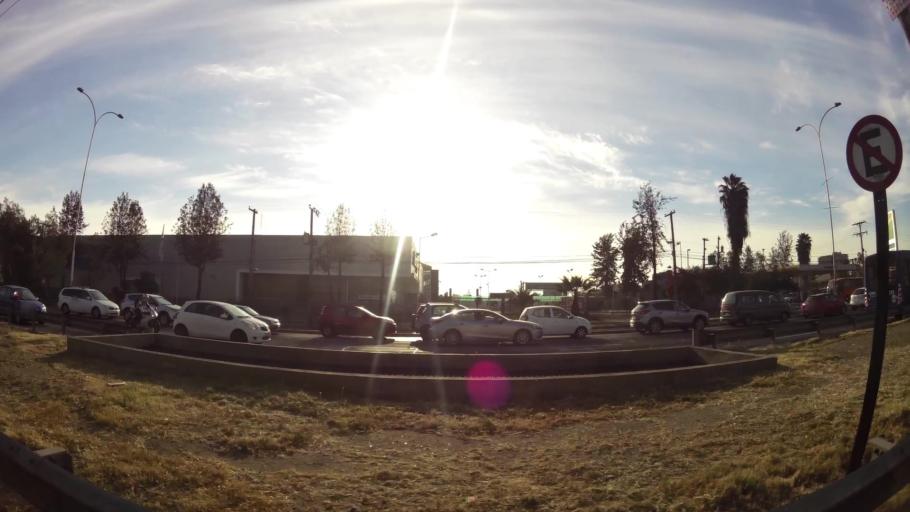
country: CL
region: Santiago Metropolitan
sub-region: Provincia de Santiago
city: Villa Presidente Frei, Nunoa, Santiago, Chile
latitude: -33.4633
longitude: -70.5740
